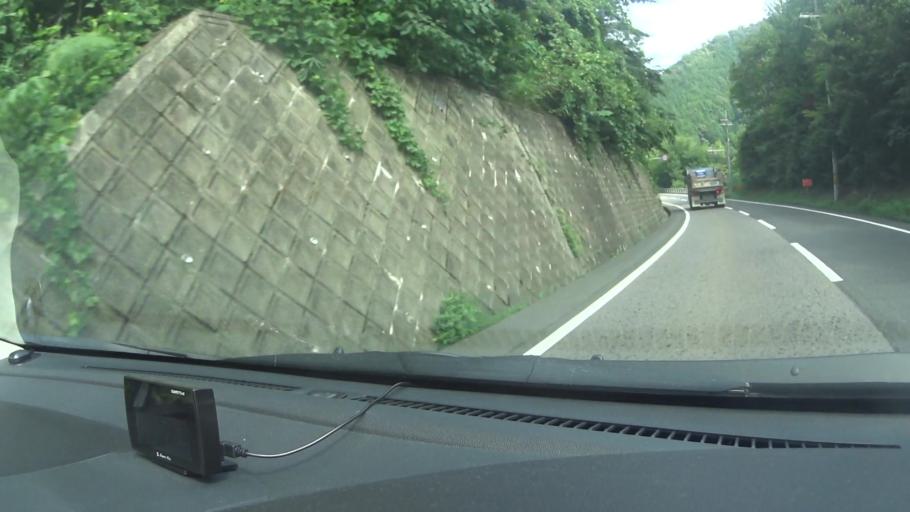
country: JP
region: Kyoto
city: Ayabe
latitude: 35.2804
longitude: 135.2697
